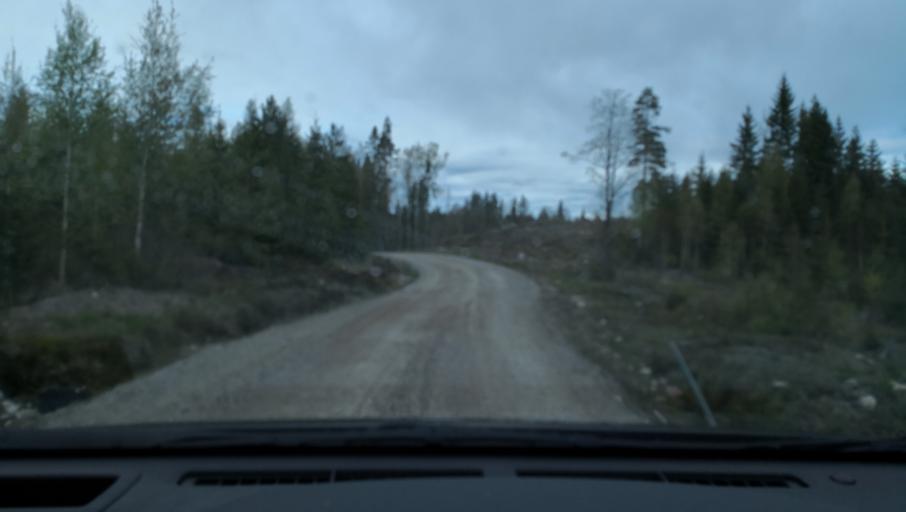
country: SE
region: Dalarna
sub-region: Saters Kommun
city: Saeter
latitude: 60.1998
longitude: 15.7451
